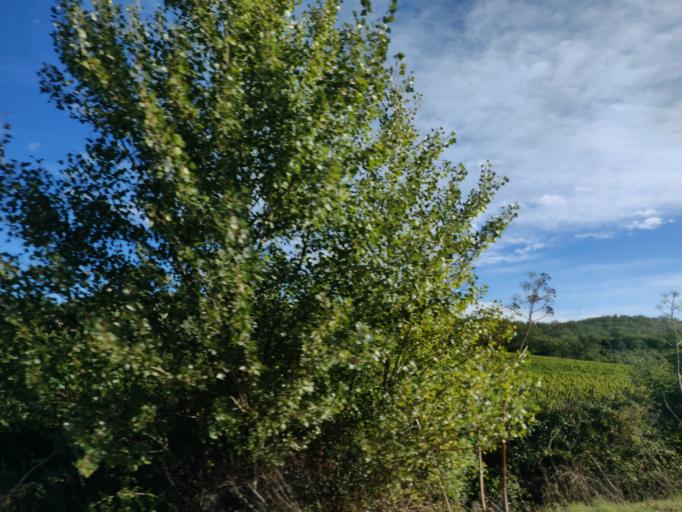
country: IT
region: Tuscany
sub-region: Provincia di Grosseto
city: Gavorrano
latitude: 42.9198
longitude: 10.9651
